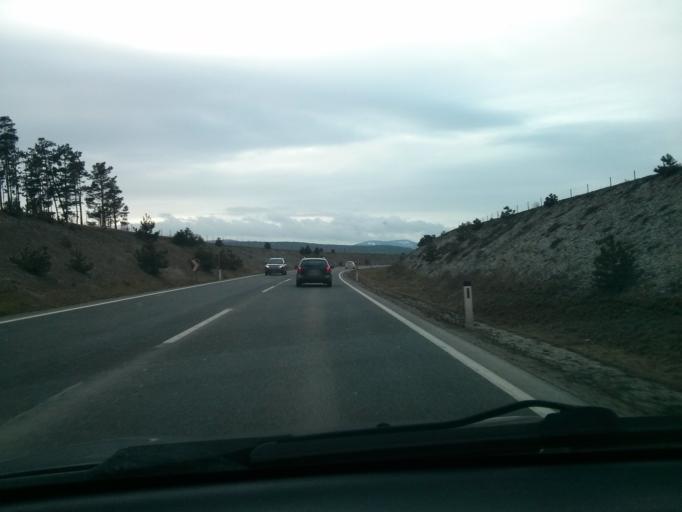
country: AT
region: Lower Austria
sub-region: Politischer Bezirk Wiener Neustadt
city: Theresienfeld
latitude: 47.8487
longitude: 16.2273
